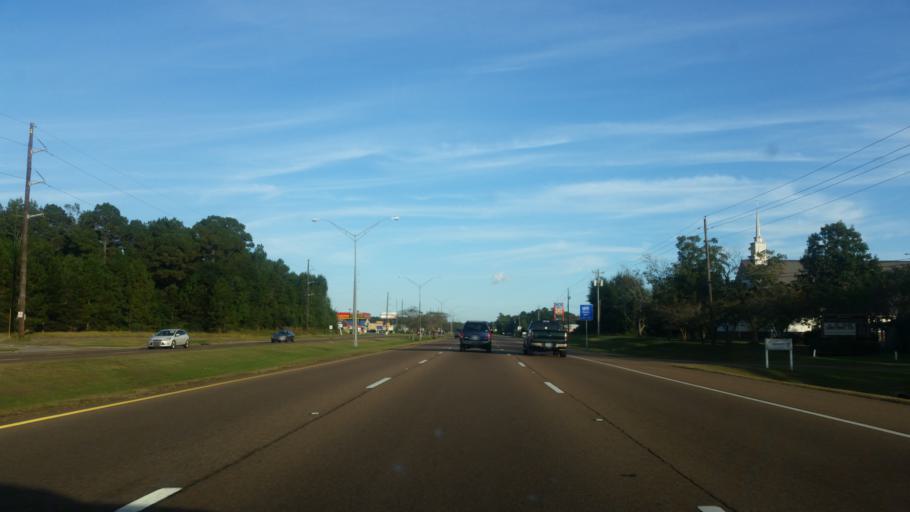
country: US
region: Mississippi
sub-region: Jackson County
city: Gautier
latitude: 30.3869
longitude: -88.6262
